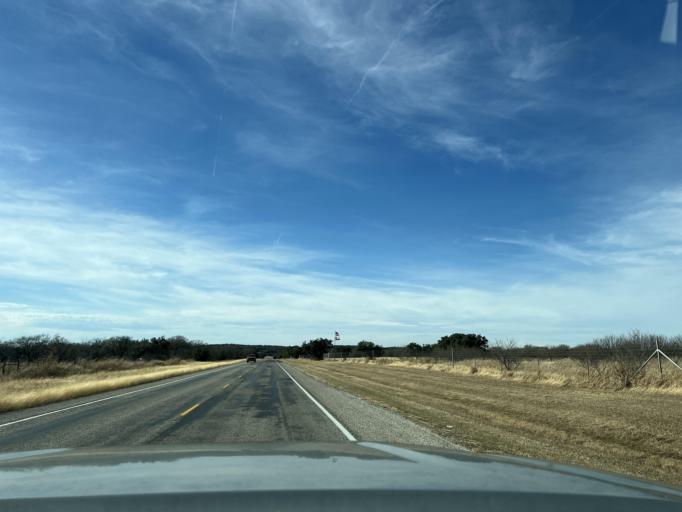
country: US
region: Texas
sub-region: Eastland County
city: Cisco
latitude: 32.4599
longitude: -98.9994
